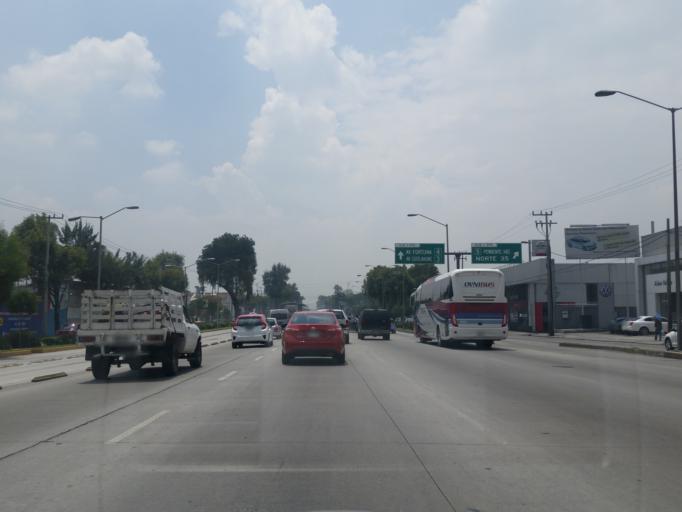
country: MX
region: Mexico
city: Colonia Lindavista
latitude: 19.4982
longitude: -99.1554
